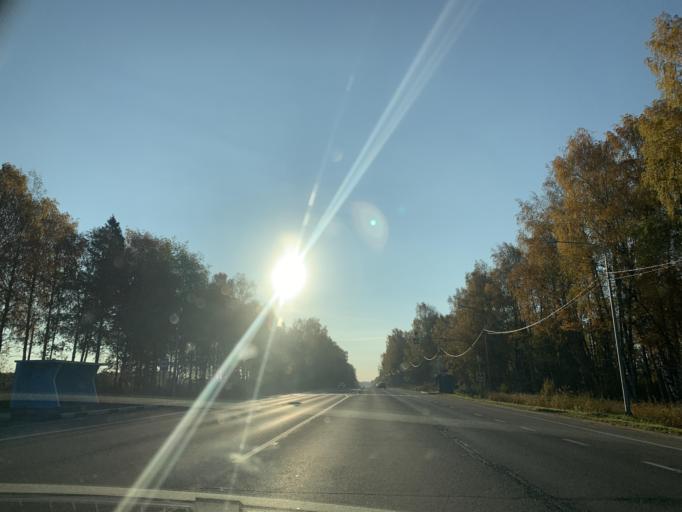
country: RU
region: Jaroslavl
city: Konstantinovskiy
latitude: 57.7520
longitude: 39.6999
